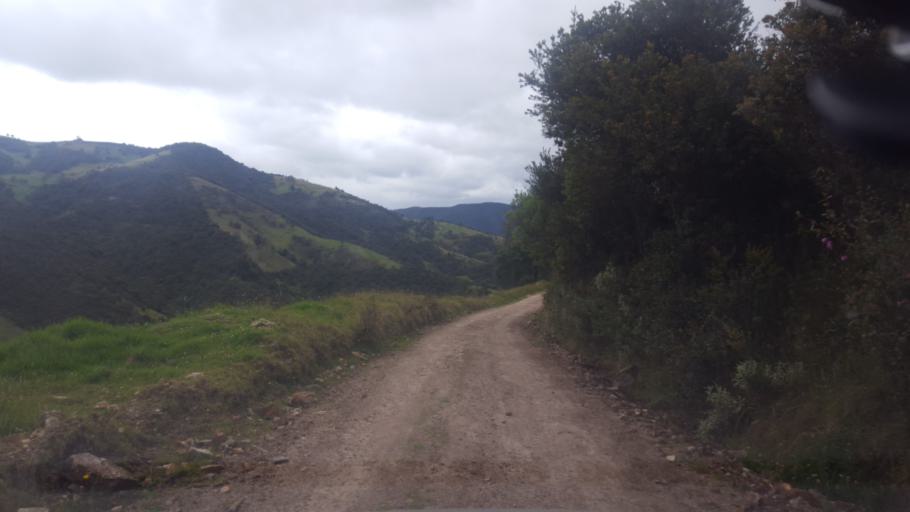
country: CO
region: Boyaca
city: Belen
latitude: 6.0313
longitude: -72.8834
